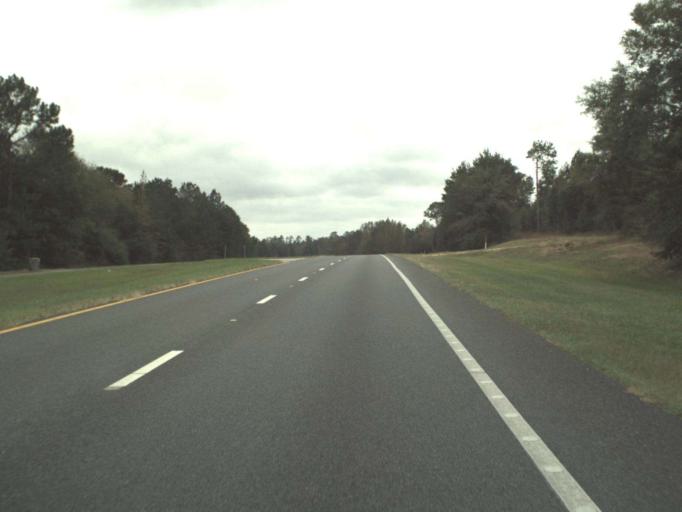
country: US
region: Florida
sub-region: Escambia County
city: Century
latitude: 30.8573
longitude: -87.3233
